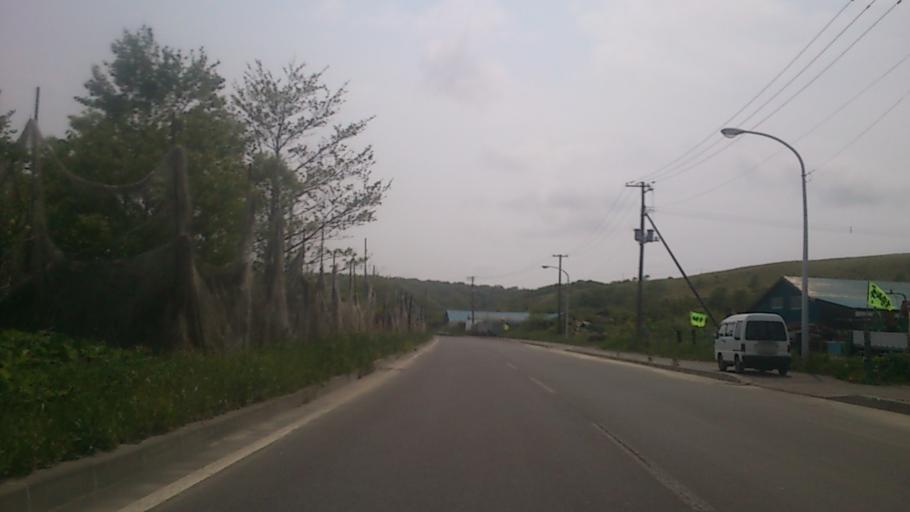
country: JP
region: Hokkaido
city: Nemuro
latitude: 43.2827
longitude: 145.5654
